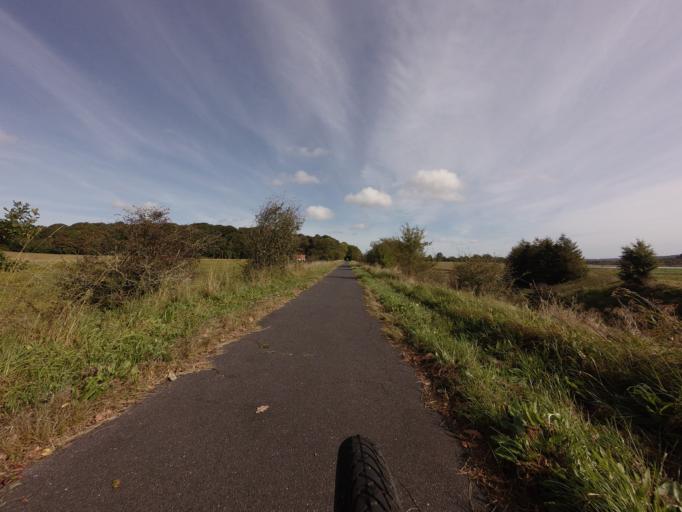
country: DK
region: Central Jutland
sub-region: Viborg Kommune
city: Bjerringbro
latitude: 56.4477
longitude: 9.5764
